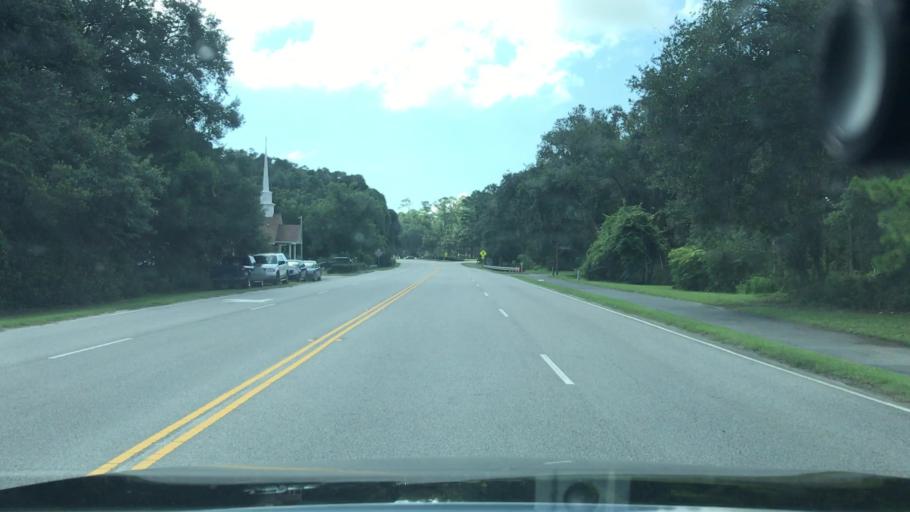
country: US
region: South Carolina
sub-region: Beaufort County
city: Hilton Head Island
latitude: 32.2043
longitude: -80.7011
